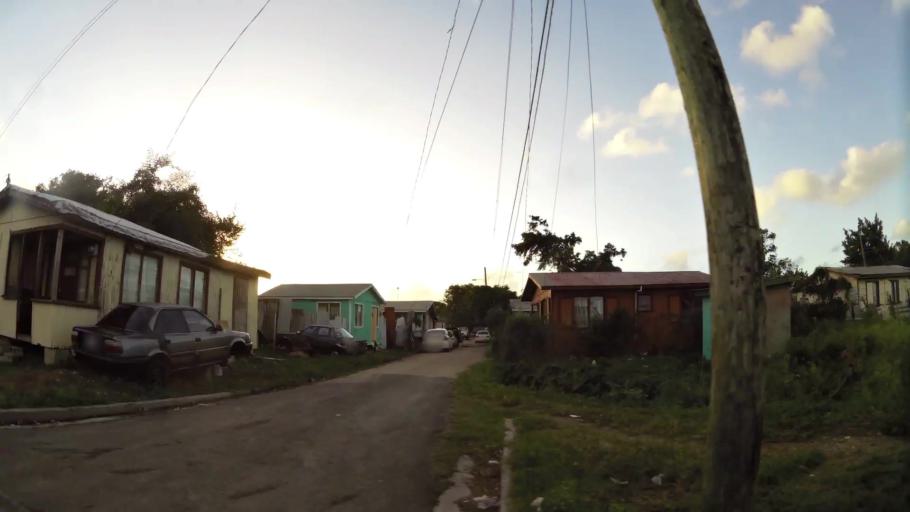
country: AG
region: Saint John
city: Saint John's
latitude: 17.1341
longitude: -61.8420
